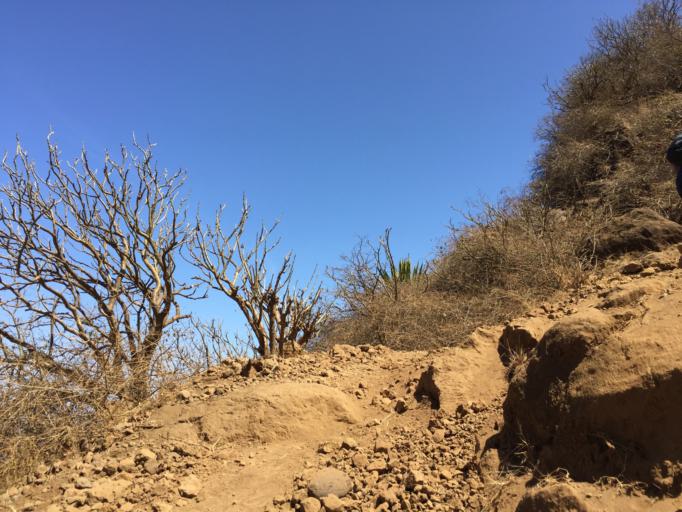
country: CV
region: Mosteiros
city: Porto dos Mosteiros
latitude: 15.0079
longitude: -24.3905
